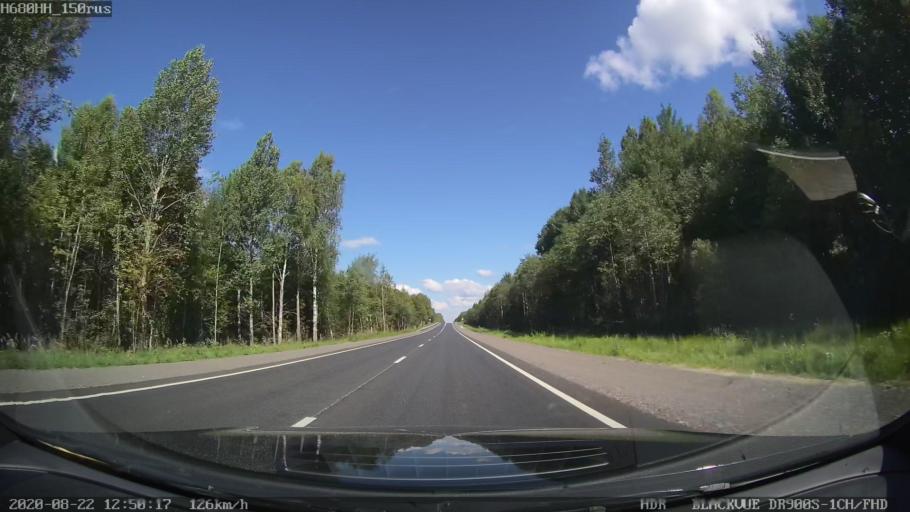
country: RU
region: Tverskaya
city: Rameshki
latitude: 57.4642
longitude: 36.2209
